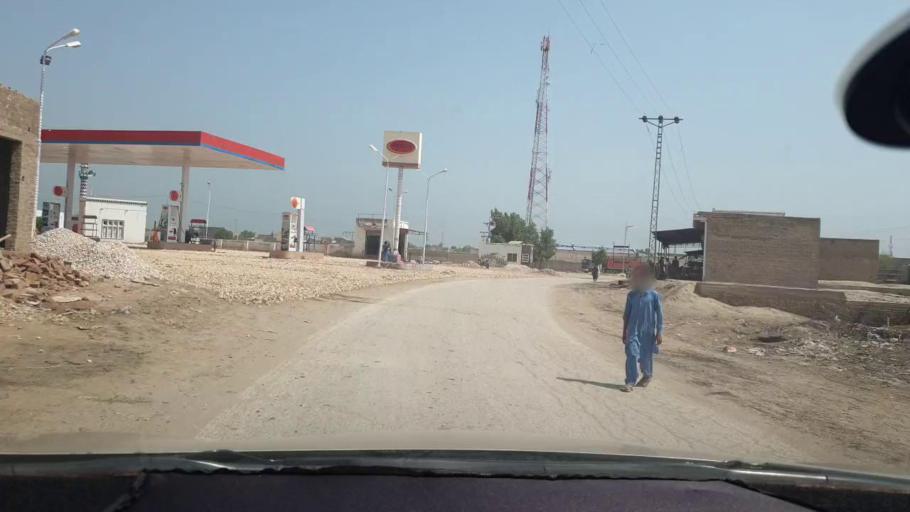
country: PK
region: Sindh
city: Kambar
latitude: 27.5920
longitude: 67.9925
